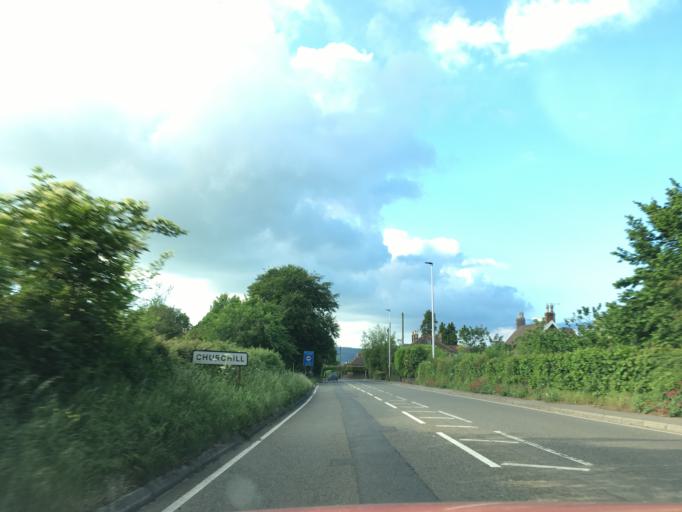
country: GB
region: England
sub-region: North Somerset
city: Churchill
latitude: 51.3310
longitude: -2.7951
